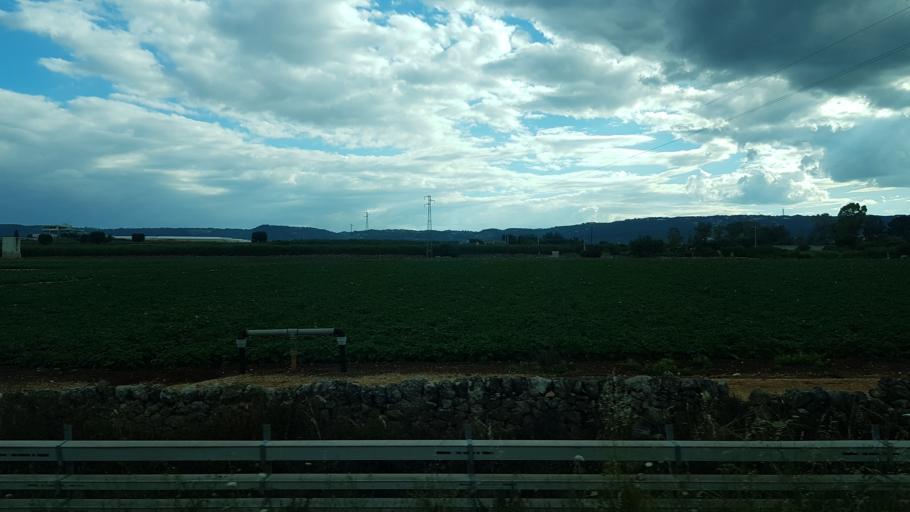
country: IT
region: Apulia
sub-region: Provincia di Brindisi
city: Fasano
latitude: 40.8486
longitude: 17.3903
